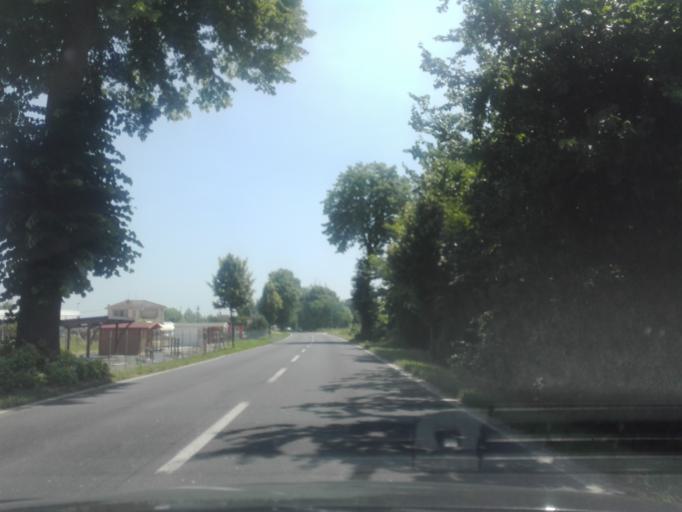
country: IT
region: Veneto
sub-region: Provincia di Rovigo
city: Adria
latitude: 45.0615
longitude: 12.0221
